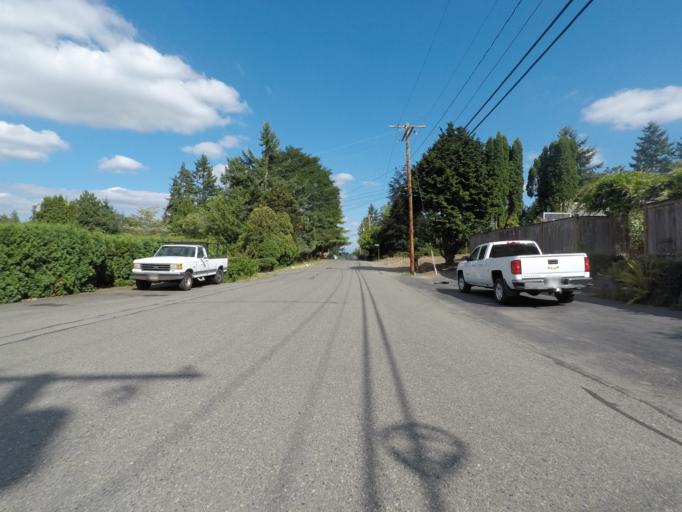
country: US
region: Washington
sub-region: King County
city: Kenmore
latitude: 47.7707
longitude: -122.2565
